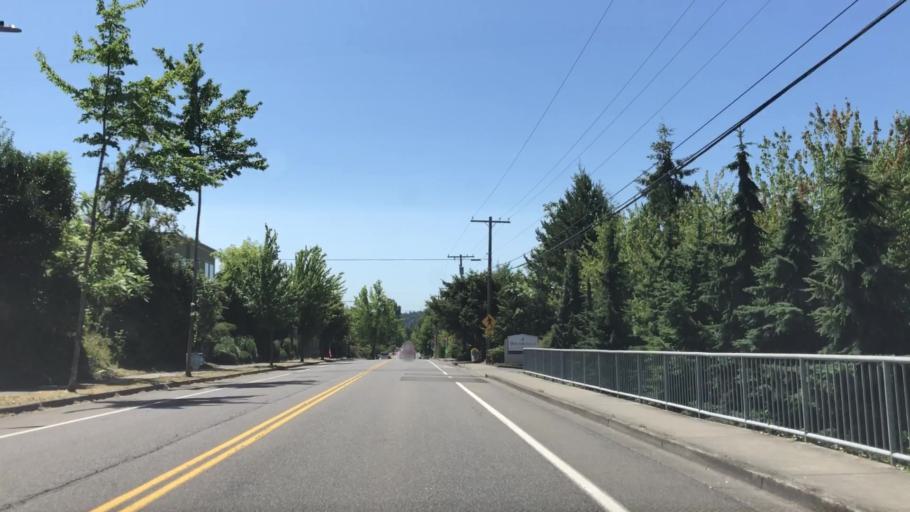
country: US
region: Washington
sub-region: King County
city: Kirkland
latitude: 47.6649
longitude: -122.2048
